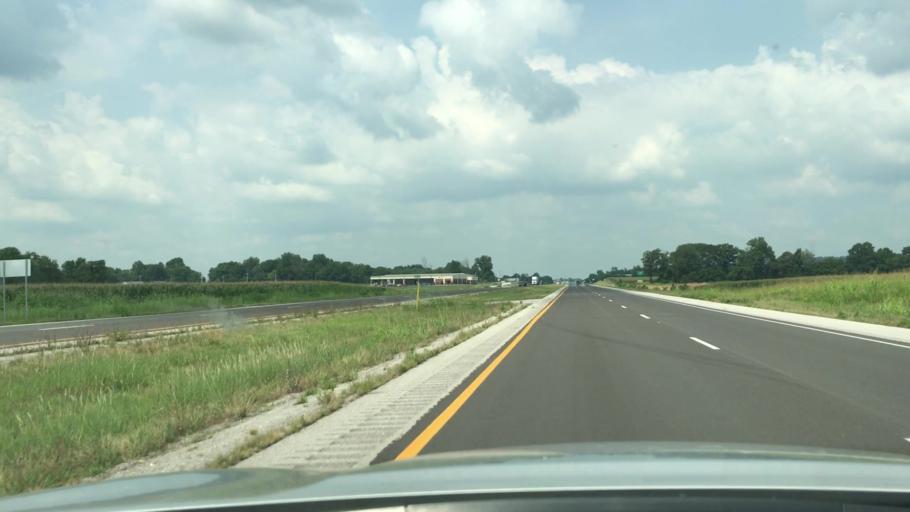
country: US
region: Kentucky
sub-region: Todd County
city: Elkton
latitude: 36.8056
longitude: -87.0570
